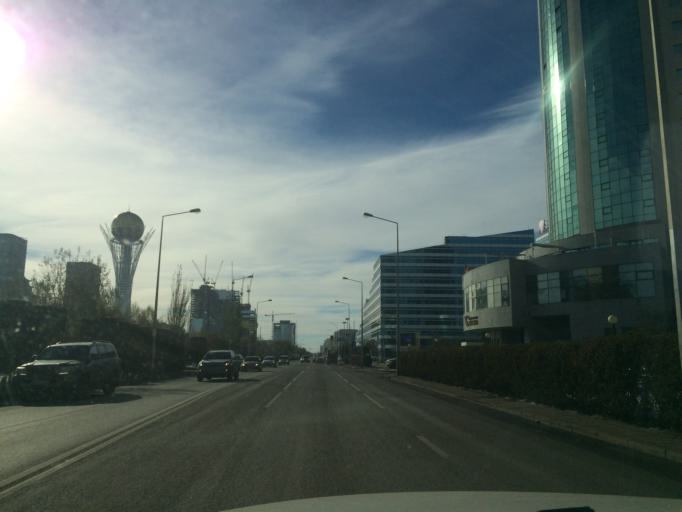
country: KZ
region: Astana Qalasy
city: Astana
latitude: 51.1322
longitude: 71.4301
